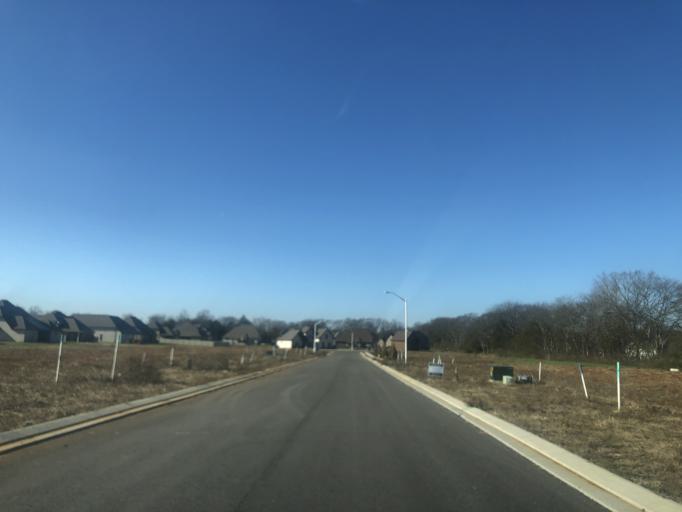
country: US
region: Tennessee
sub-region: Rutherford County
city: Smyrna
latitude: 35.8977
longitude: -86.4797
